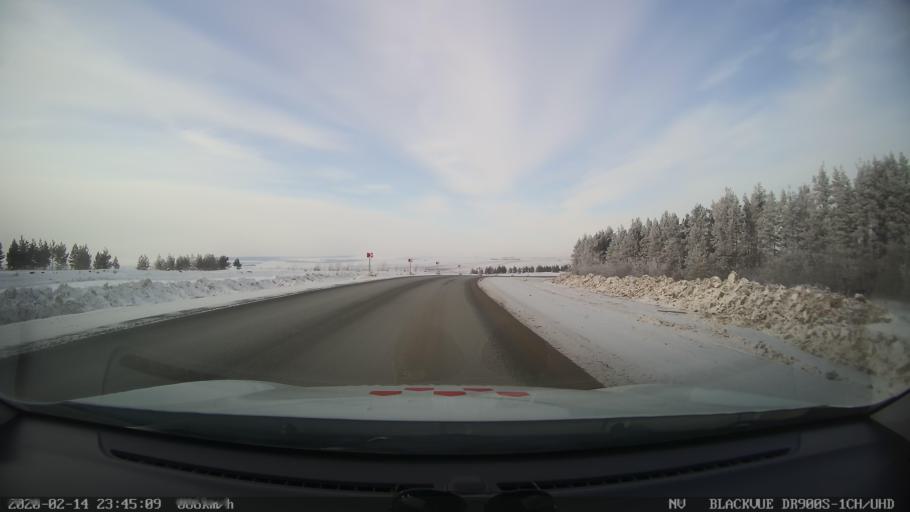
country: RU
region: Tatarstan
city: Kuybyshevskiy Zaton
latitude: 55.2168
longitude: 49.2332
